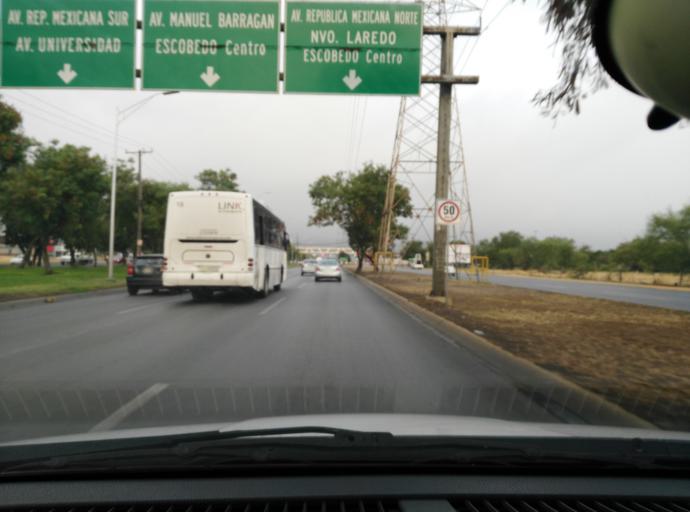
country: MX
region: Nuevo Leon
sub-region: San Nicolas de los Garza
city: San Nicolas de los Garza
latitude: 25.7705
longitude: -100.2692
